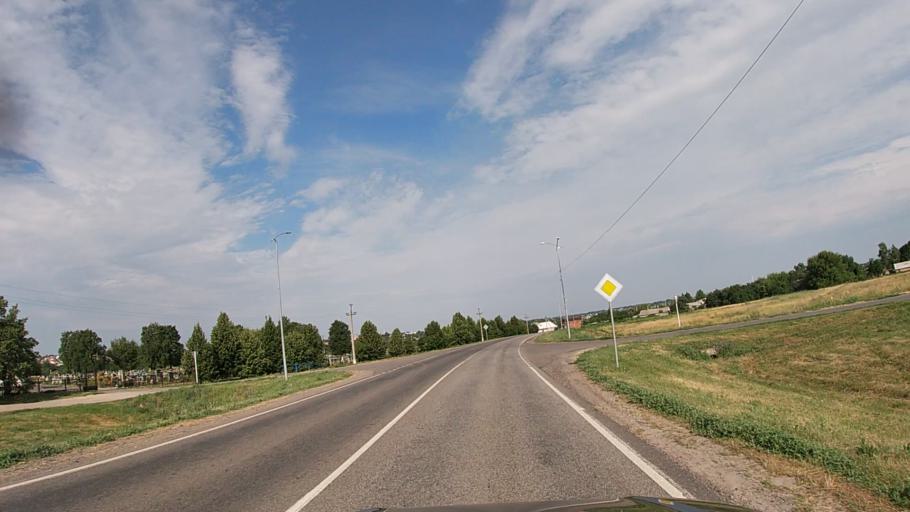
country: RU
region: Belgorod
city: Krasnaya Yaruga
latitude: 50.7985
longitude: 35.6802
